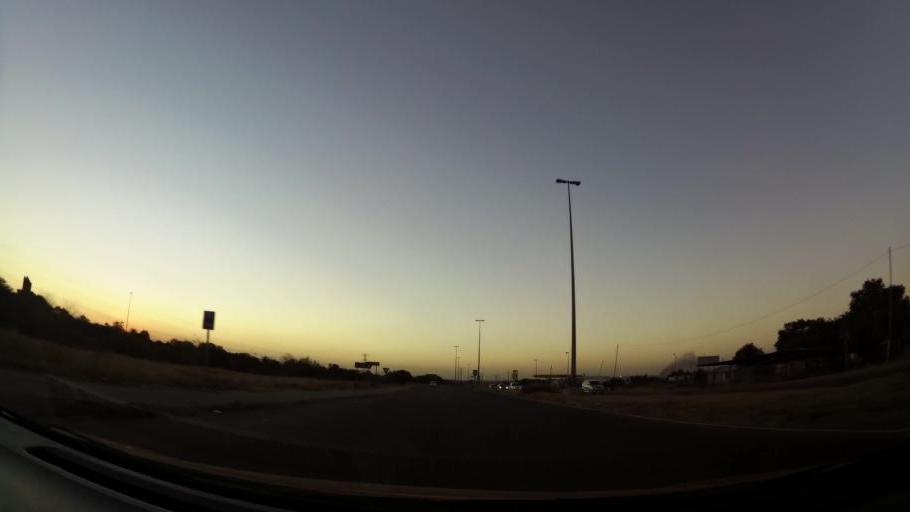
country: ZA
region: North-West
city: Ga-Rankuwa
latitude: -25.5988
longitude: 27.9908
